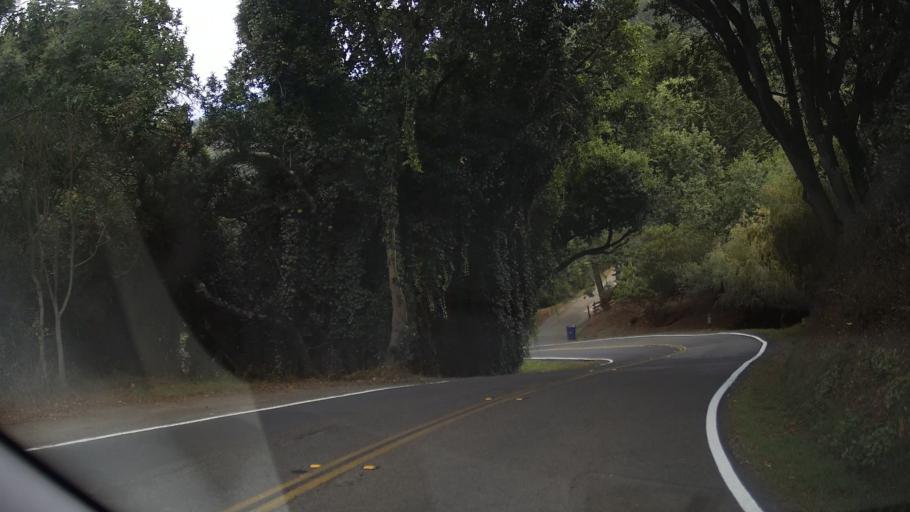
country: US
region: California
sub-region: Marin County
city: Bolinas
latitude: 37.8979
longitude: -122.6326
